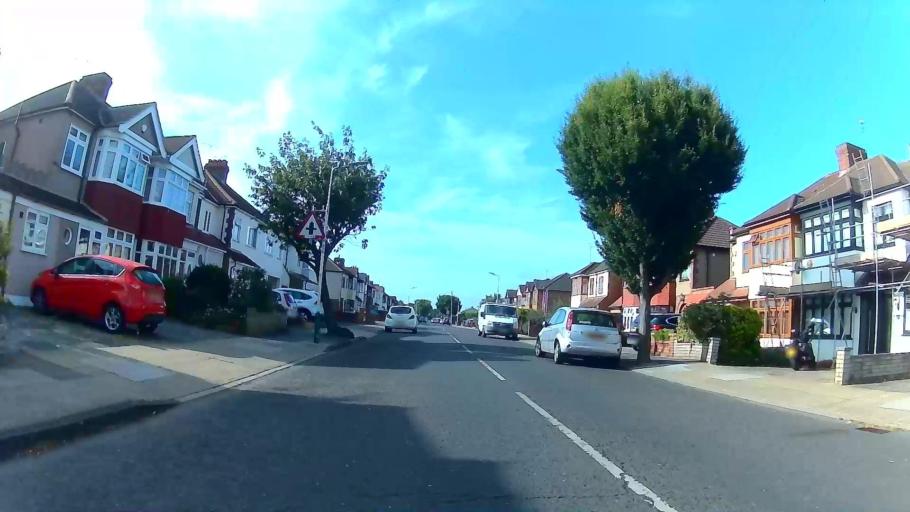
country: GB
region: England
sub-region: Greater London
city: Elm Park
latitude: 51.5624
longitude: 0.1955
